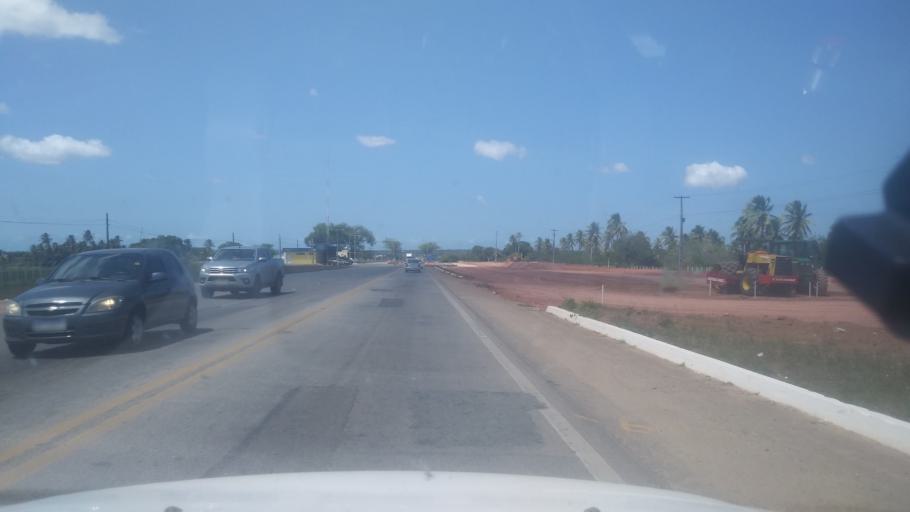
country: BR
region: Rio Grande do Norte
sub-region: Macaiba
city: Macaiba
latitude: -5.8680
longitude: -35.3726
